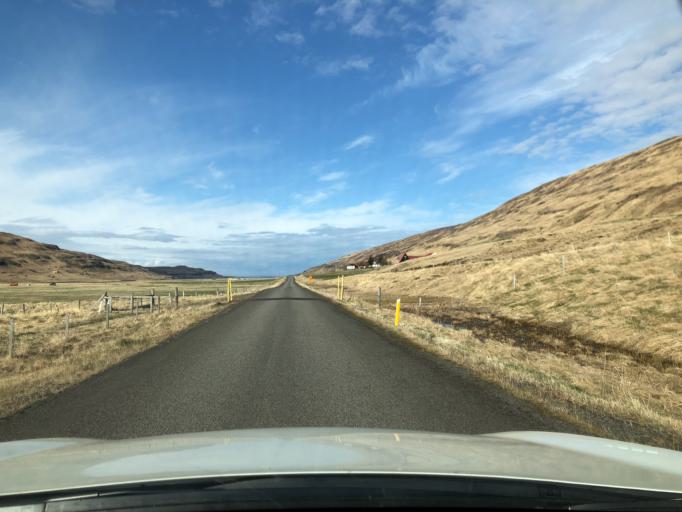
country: IS
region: West
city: Borgarnes
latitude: 65.0582
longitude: -21.5386
